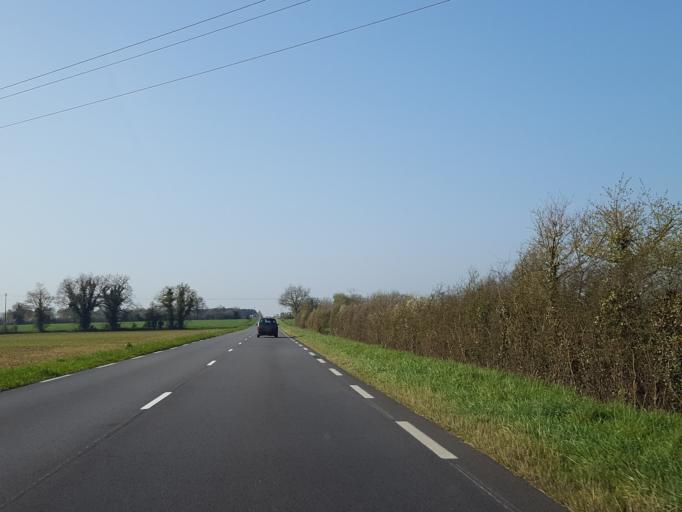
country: FR
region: Pays de la Loire
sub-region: Departement de la Vendee
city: Saint-Philbert-de-Bouaine
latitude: 47.0059
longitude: -1.5080
